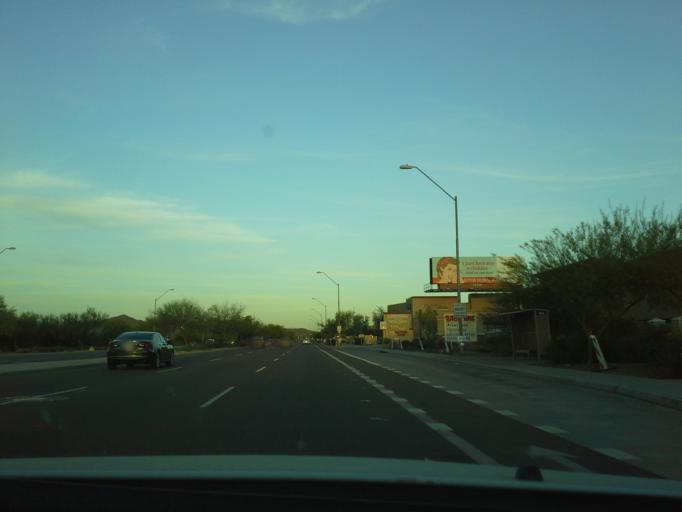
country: US
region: Arizona
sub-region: Maricopa County
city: Anthem
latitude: 33.7128
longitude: -112.1085
